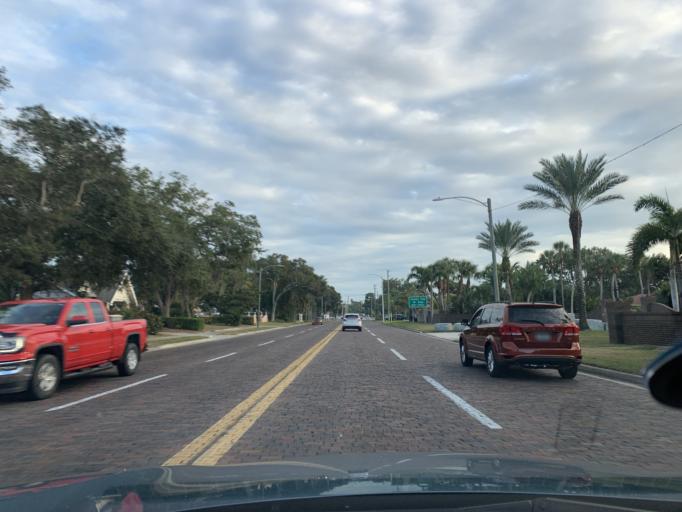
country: US
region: Florida
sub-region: Pinellas County
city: Treasure Island
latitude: 27.7812
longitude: -82.7475
